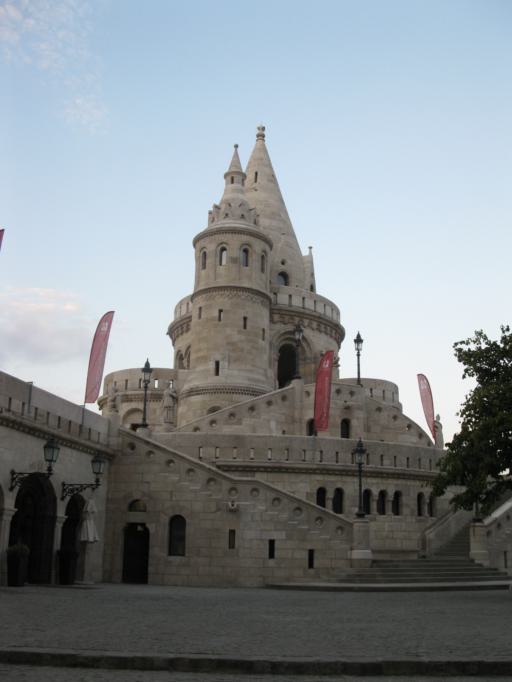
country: HU
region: Budapest
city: Budapest
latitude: 47.5026
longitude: 19.0343
